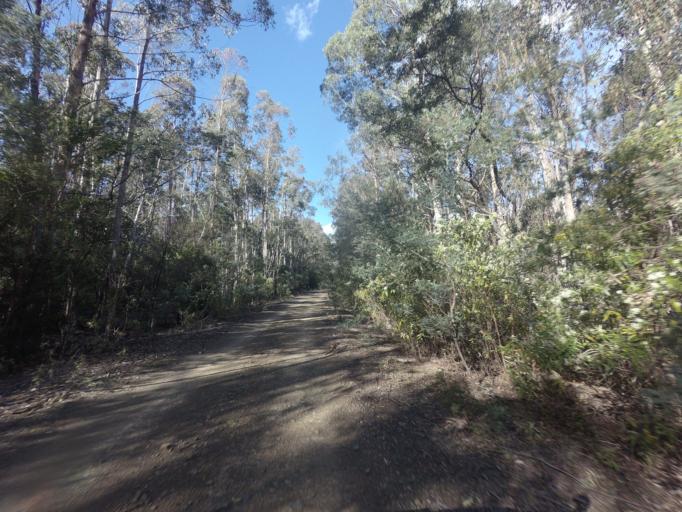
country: AU
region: Tasmania
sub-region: Break O'Day
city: St Helens
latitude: -41.8454
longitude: 148.0593
